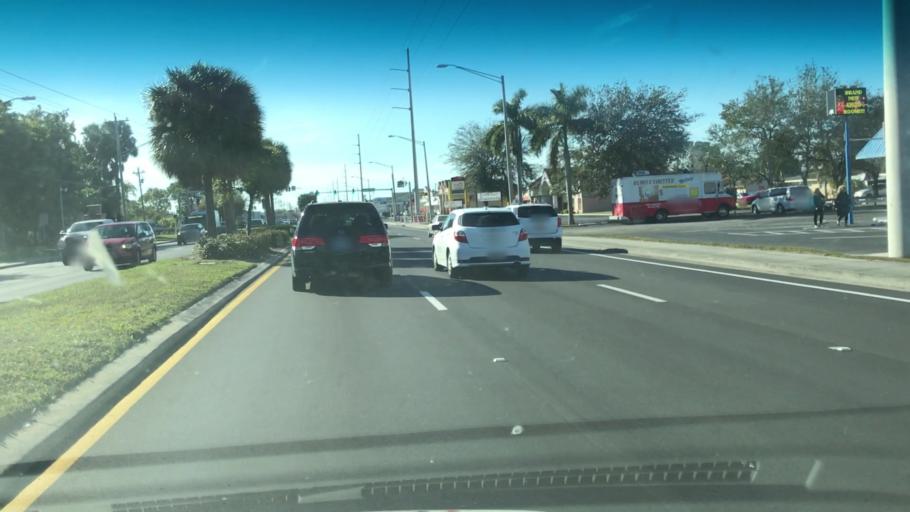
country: US
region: Florida
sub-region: Lee County
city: Cape Coral
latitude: 26.5973
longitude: -81.9417
